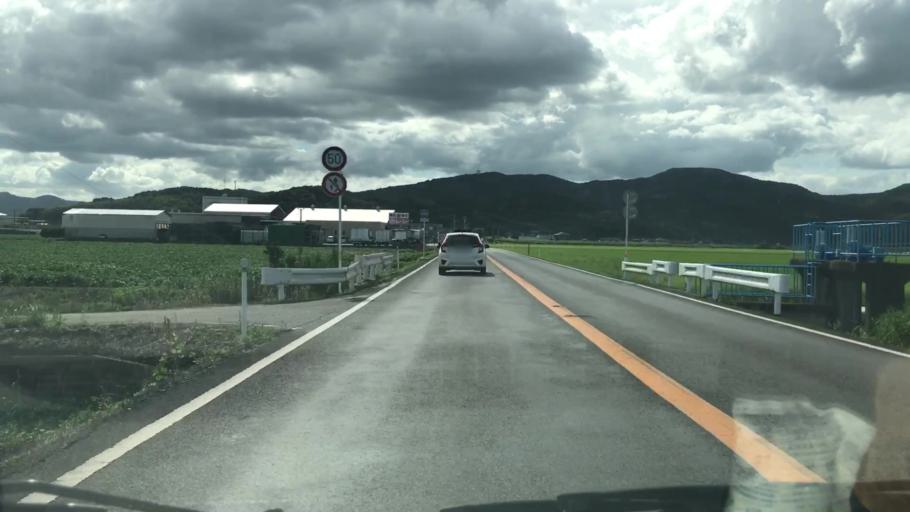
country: JP
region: Saga Prefecture
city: Kashima
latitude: 33.1398
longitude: 130.1314
